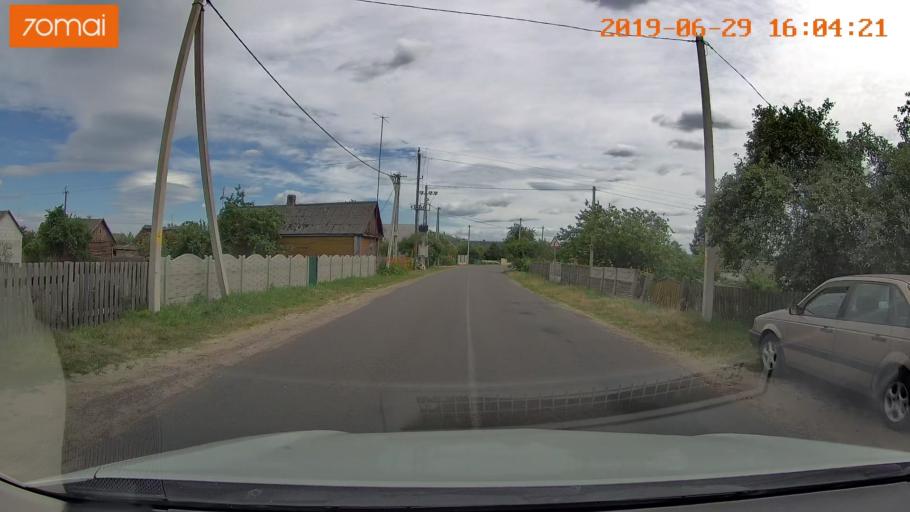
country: BY
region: Brest
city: Luninyets
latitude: 52.2233
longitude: 27.0245
